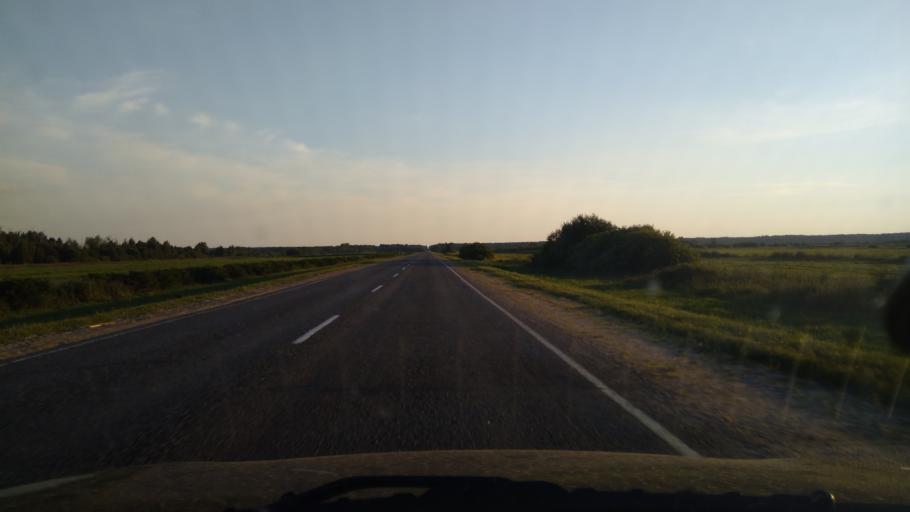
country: BY
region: Brest
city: Nyakhachava
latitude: 52.6272
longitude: 25.1713
